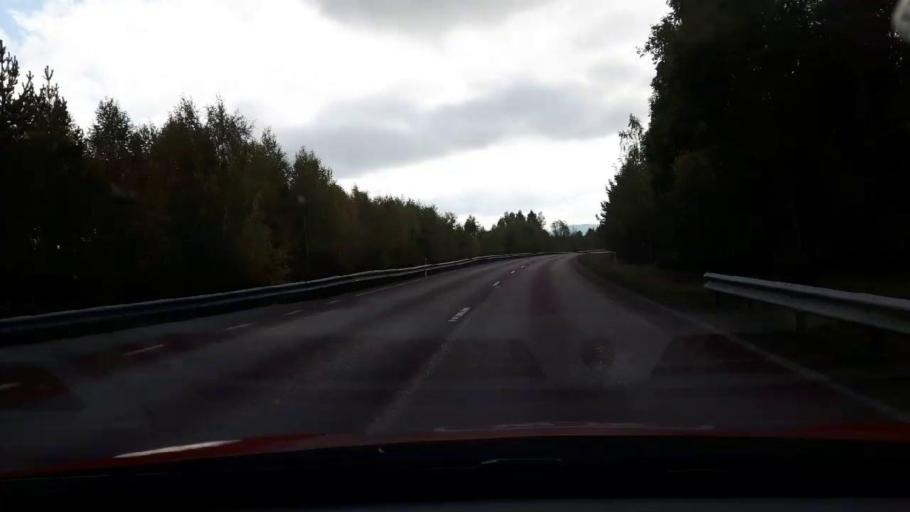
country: SE
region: Gaevleborg
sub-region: Ljusdals Kommun
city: Jaervsoe
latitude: 61.6170
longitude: 16.2939
